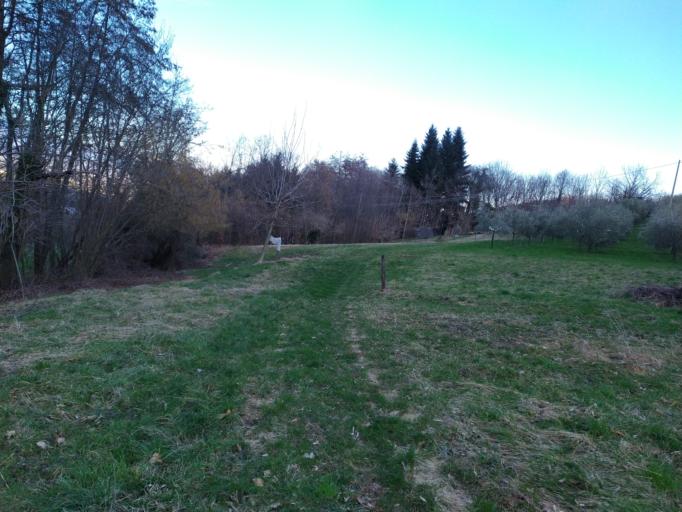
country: IT
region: Veneto
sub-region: Provincia di Vicenza
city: Monte di Malo
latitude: 45.6781
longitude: 11.3528
